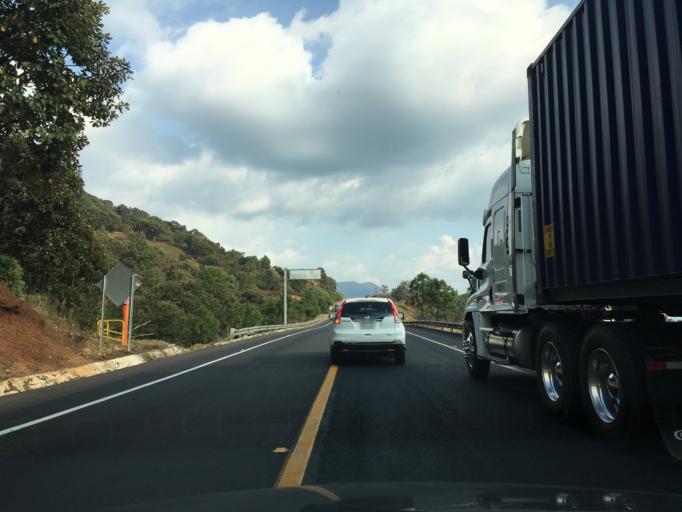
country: MX
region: Michoacan
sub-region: Ziracuaretiro
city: Patuan
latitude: 19.4335
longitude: -101.9016
